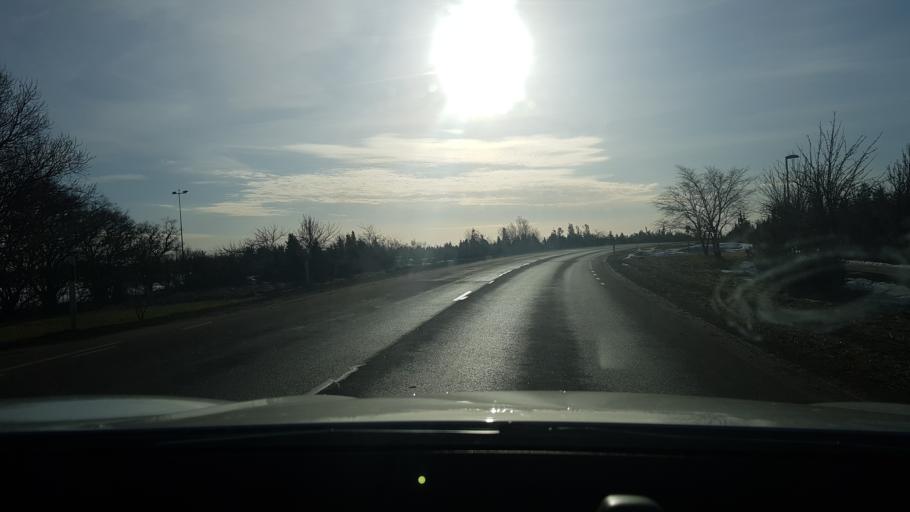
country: EE
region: Saare
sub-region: Kuressaare linn
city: Kuressaare
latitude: 58.2317
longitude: 22.5039
